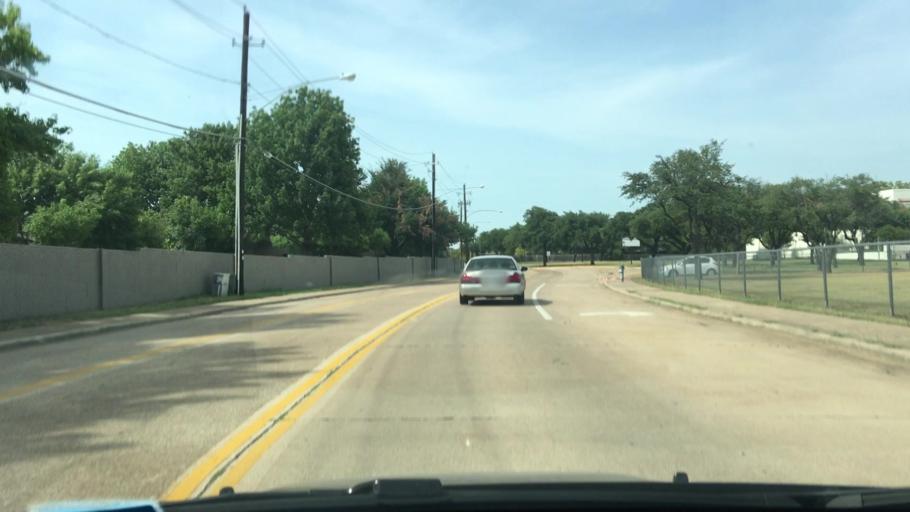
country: US
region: Texas
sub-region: Dallas County
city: Addison
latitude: 32.9188
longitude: -96.8116
